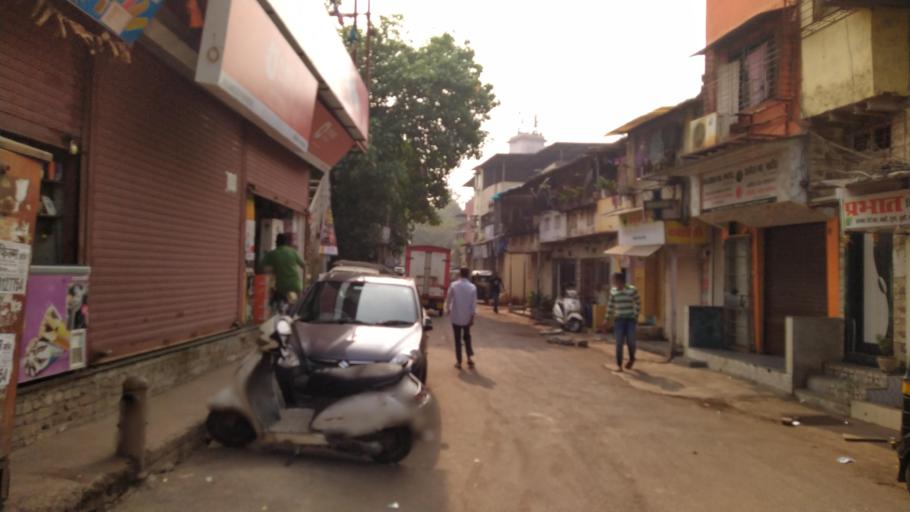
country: IN
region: Maharashtra
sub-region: Mumbai Suburban
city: Mumbai
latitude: 19.0615
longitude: 72.8738
